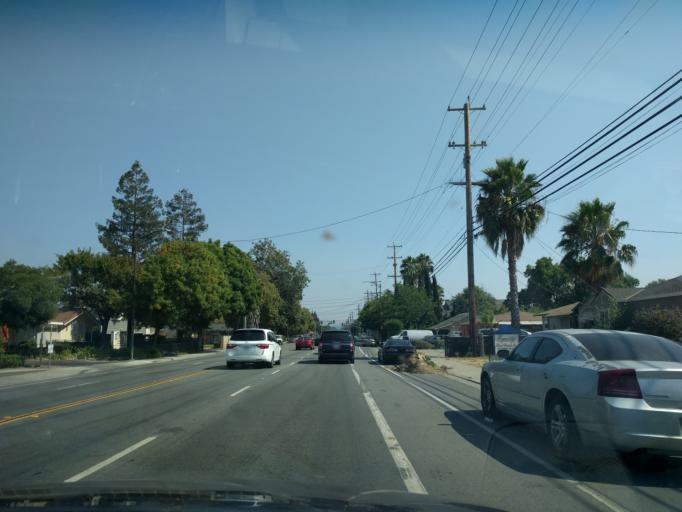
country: US
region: California
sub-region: Santa Clara County
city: Alum Rock
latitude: 37.3613
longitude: -121.8239
